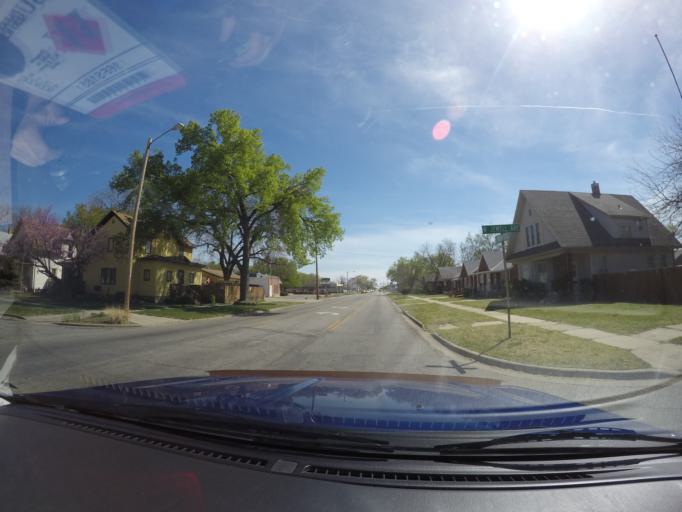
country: US
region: Kansas
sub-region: Saline County
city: Salina
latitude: 38.8163
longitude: -97.6128
